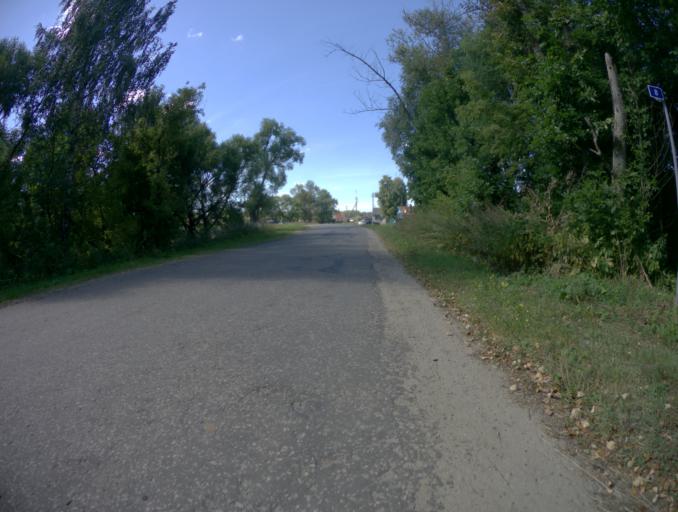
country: RU
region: Vladimir
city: Dobryatino
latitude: 55.6745
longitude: 41.3702
